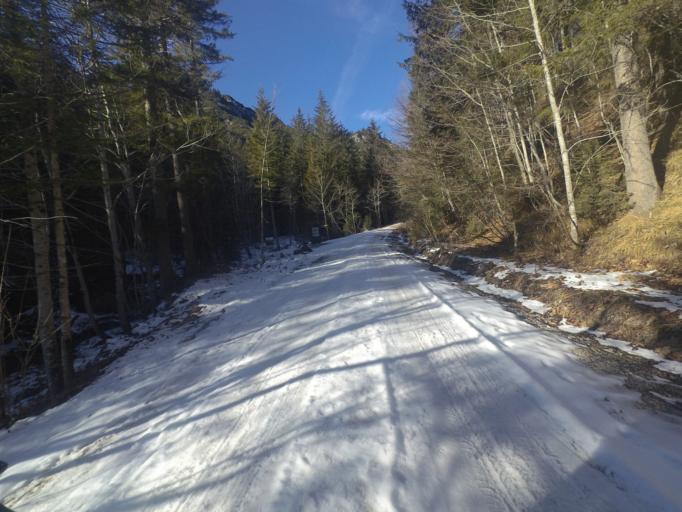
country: AT
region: Salzburg
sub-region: Politischer Bezirk Salzburg-Umgebung
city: Strobl
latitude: 47.6019
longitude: 13.4588
